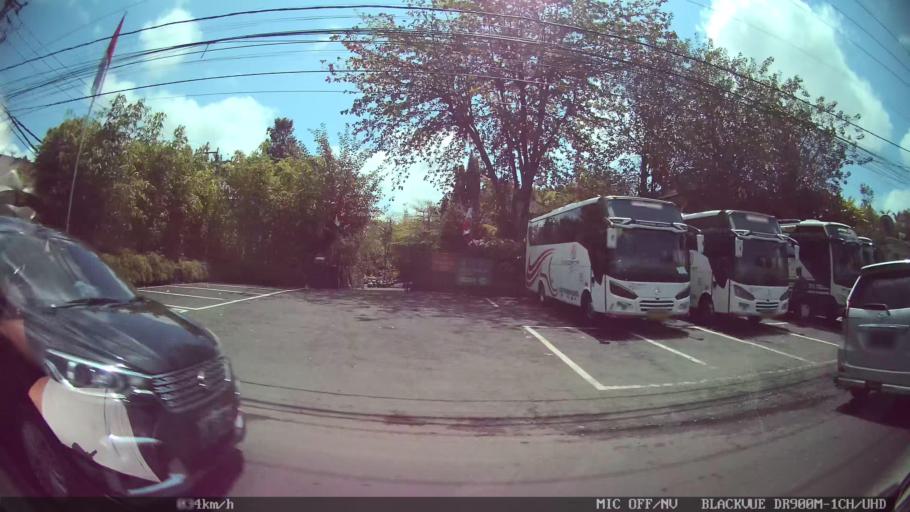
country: ID
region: Bali
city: Banjar Jabejero
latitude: -8.5920
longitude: 115.2661
